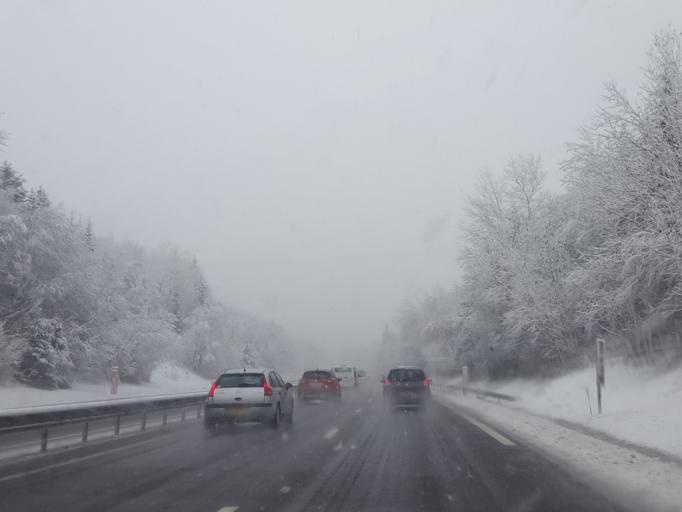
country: FR
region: Rhone-Alpes
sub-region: Departement de la Haute-Savoie
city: Etaux
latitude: 46.0519
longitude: 6.2875
